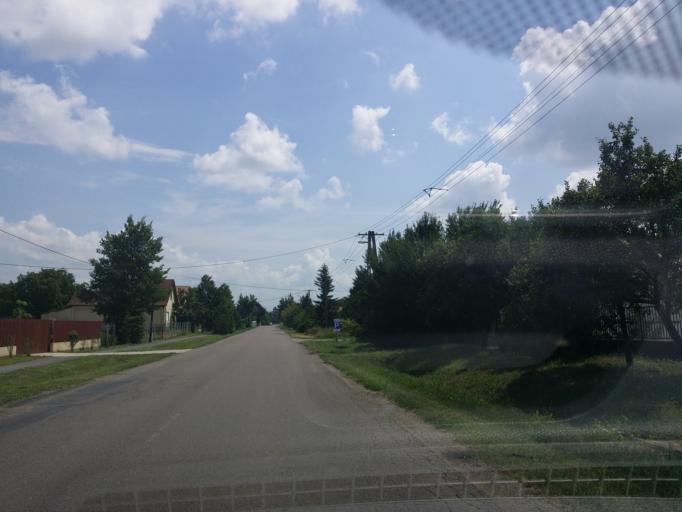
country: HU
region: Heves
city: Tiszanana
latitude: 47.6016
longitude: 20.5853
